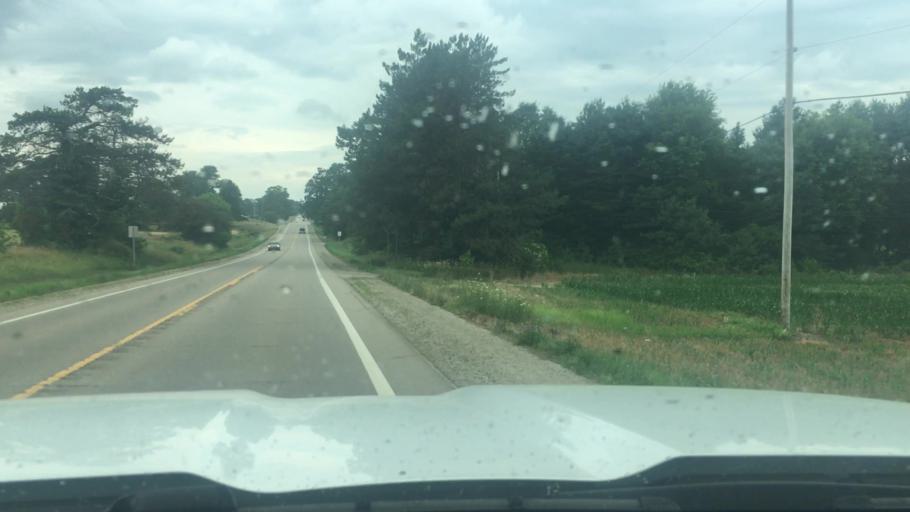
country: US
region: Michigan
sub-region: Ionia County
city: Ionia
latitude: 43.0019
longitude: -84.9870
